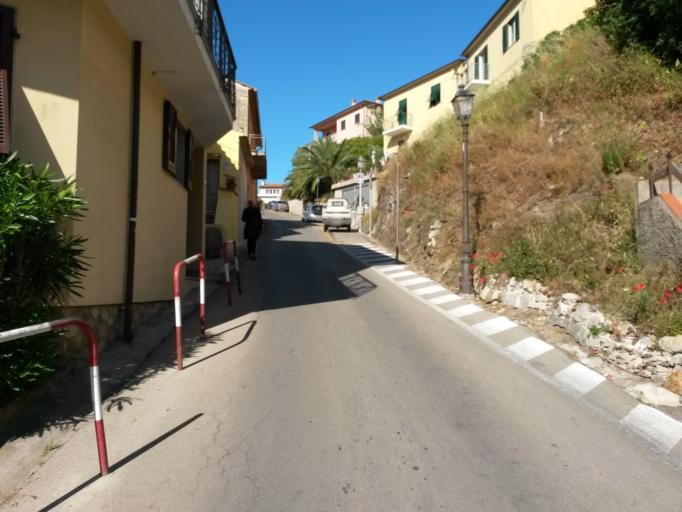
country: IT
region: Tuscany
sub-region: Provincia di Livorno
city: Porto Azzurro
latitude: 42.7663
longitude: 10.3990
